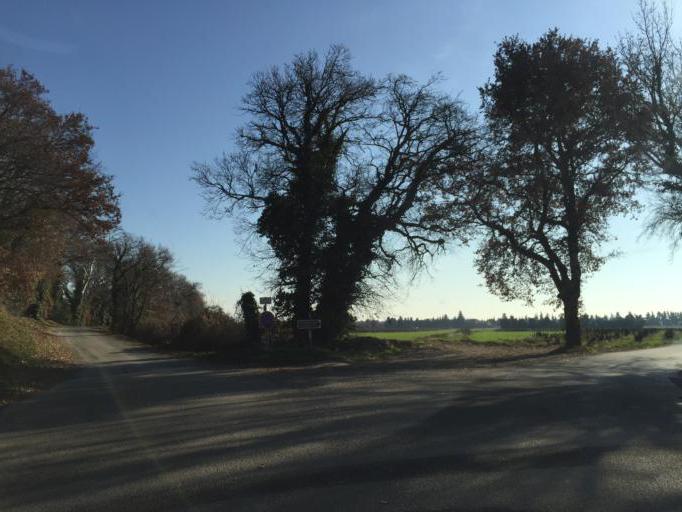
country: FR
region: Provence-Alpes-Cote d'Azur
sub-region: Departement du Vaucluse
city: Jonquieres
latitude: 44.1015
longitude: 4.9134
